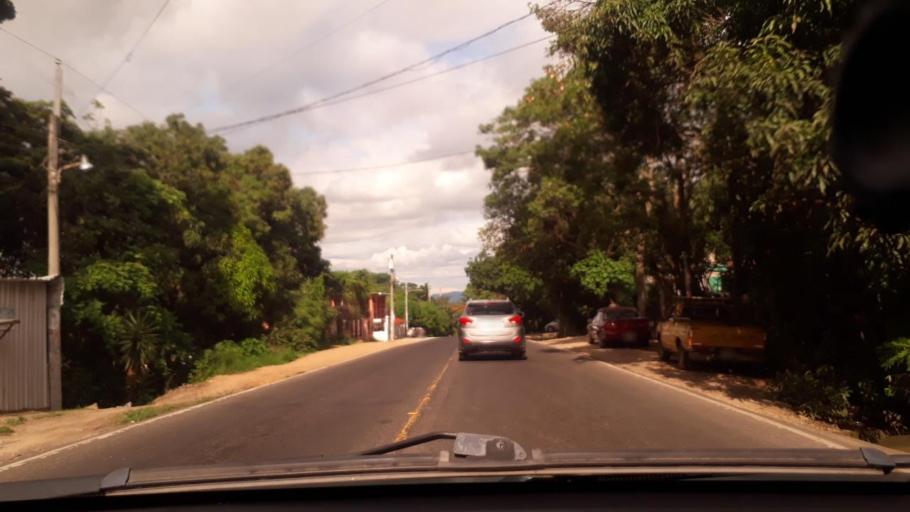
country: GT
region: Jutiapa
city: Quesada
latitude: 14.2770
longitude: -89.9830
